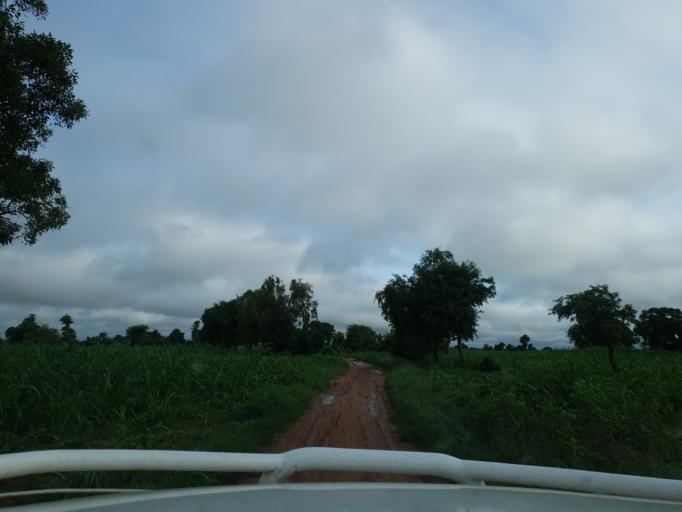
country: ML
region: Segou
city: Baroueli
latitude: 13.4007
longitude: -7.0064
